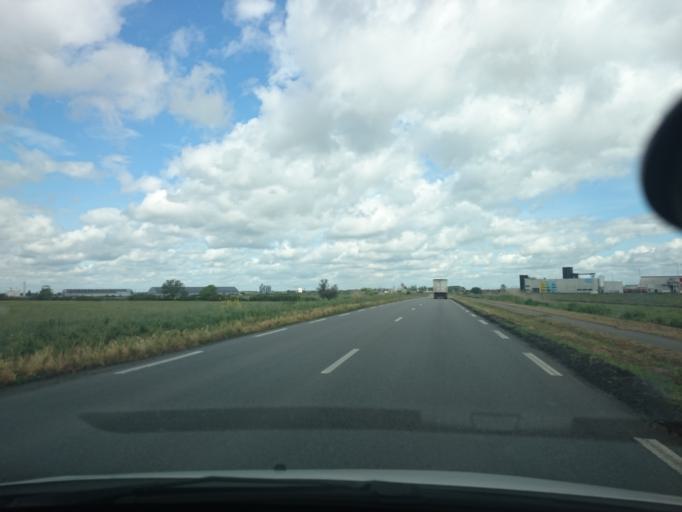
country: FR
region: Pays de la Loire
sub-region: Departement de la Loire-Atlantique
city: Montoir-de-Bretagne
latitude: 47.3135
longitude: -2.1247
